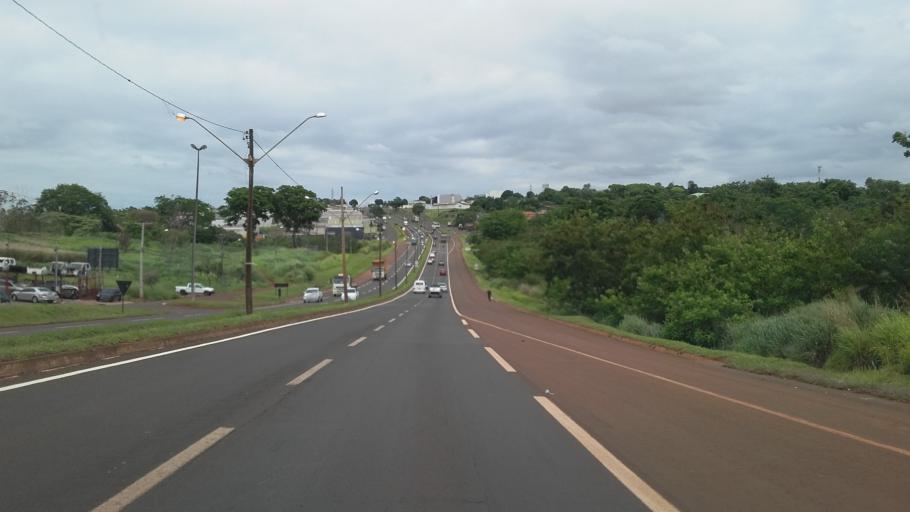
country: BR
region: Parana
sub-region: Londrina
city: Londrina
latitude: -23.2936
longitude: -51.1142
